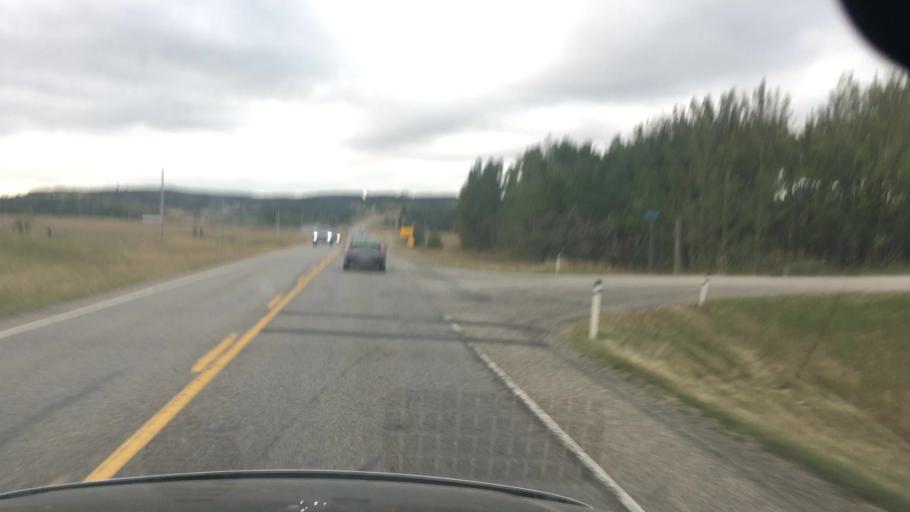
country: CA
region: Alberta
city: Cochrane
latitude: 51.3804
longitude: -114.4703
